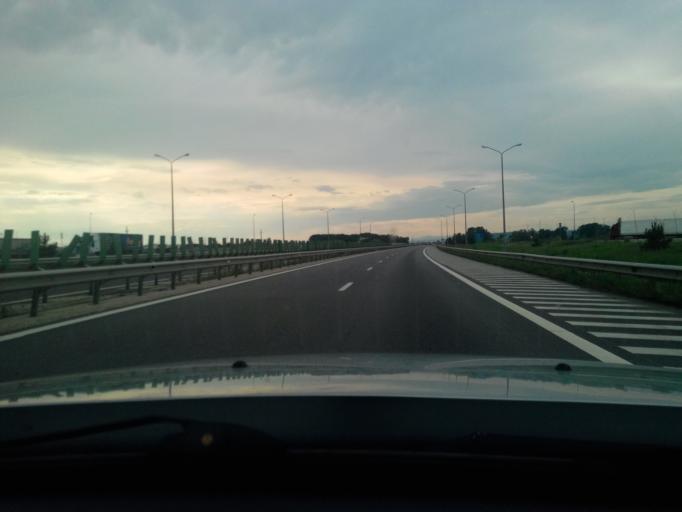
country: RO
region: Arges
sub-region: Comuna Bradu
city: Geamana
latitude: 44.8321
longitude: 24.9251
